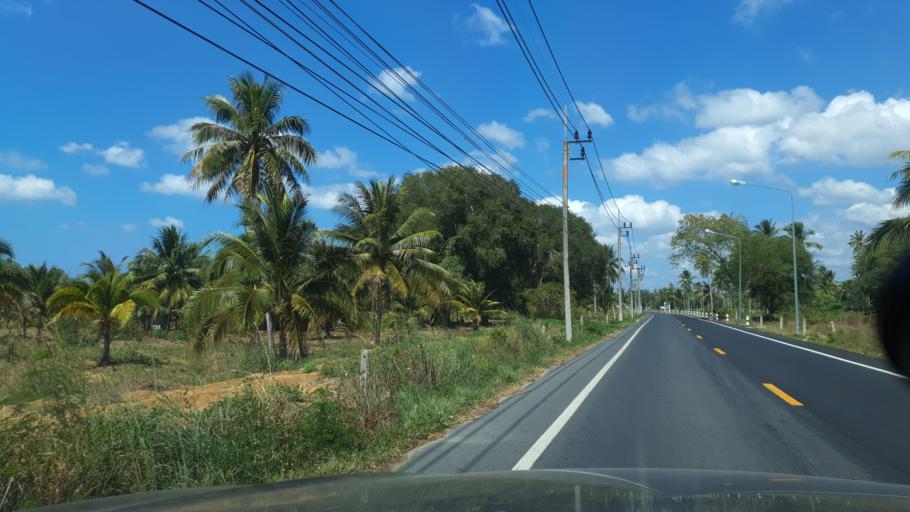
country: TH
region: Phuket
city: Thalang
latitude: 8.1470
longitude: 98.3060
